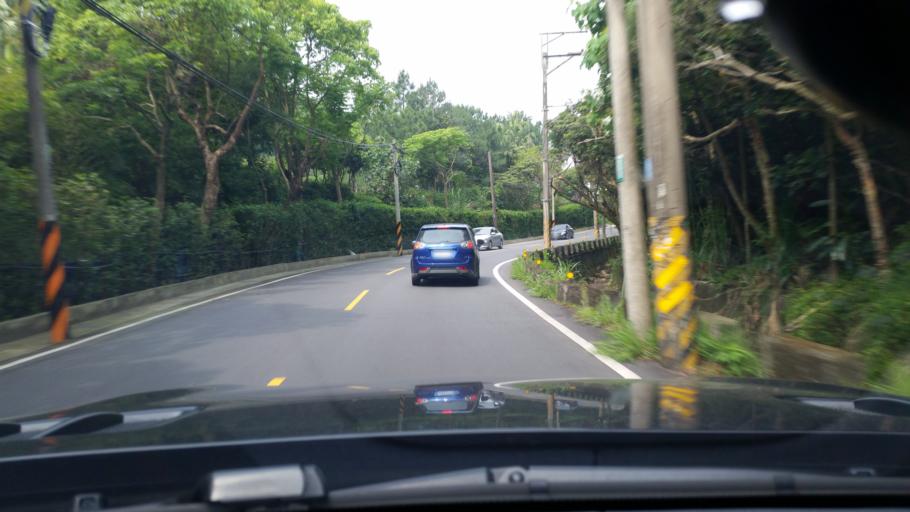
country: TW
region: Taiwan
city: Taoyuan City
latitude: 25.0612
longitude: 121.3118
